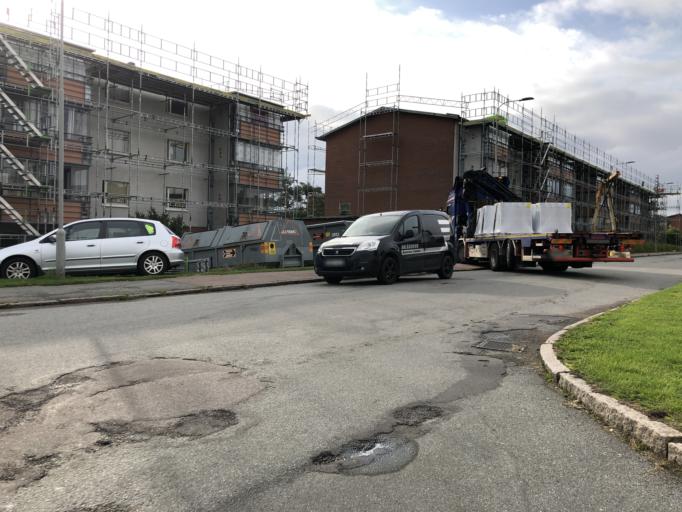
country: SE
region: Vaestra Goetaland
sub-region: Goteborg
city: Majorna
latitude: 57.7376
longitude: 11.8929
